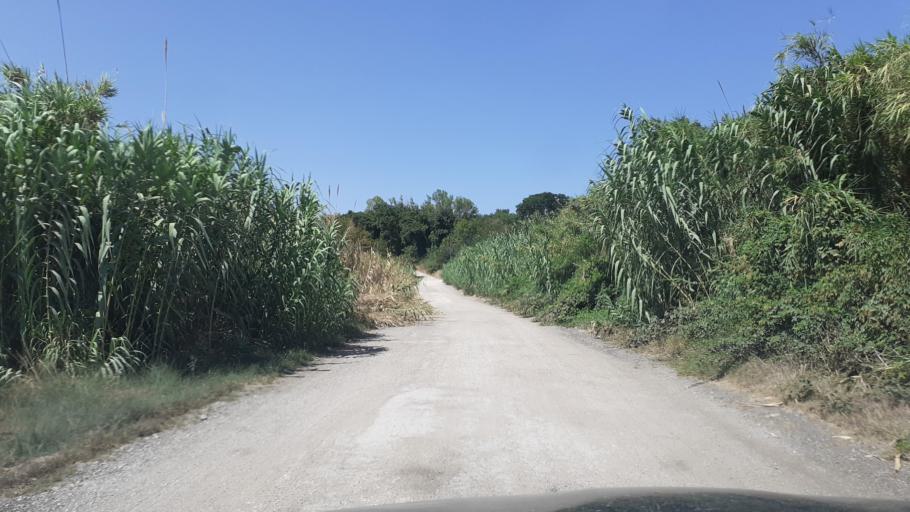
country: IT
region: Abruzzo
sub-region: Provincia di Chieti
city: Fossacesia
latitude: 42.2060
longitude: 14.4838
